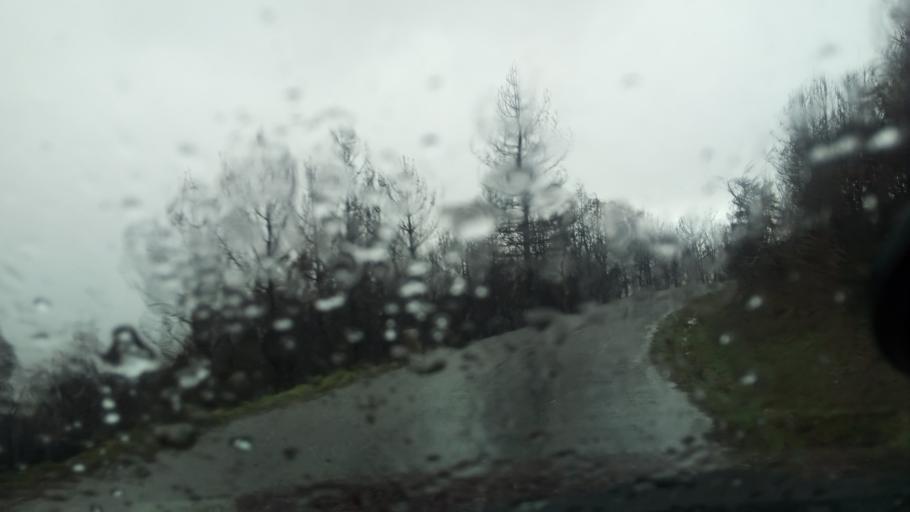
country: PT
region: Guarda
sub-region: Celorico da Beira
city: Celorico da Beira
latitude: 40.5410
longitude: -7.4488
